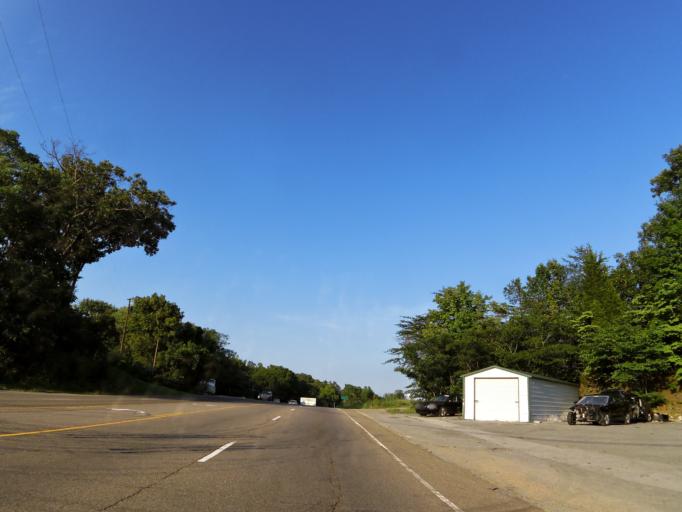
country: US
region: Tennessee
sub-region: Anderson County
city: Clinton
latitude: 36.0286
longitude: -84.0708
